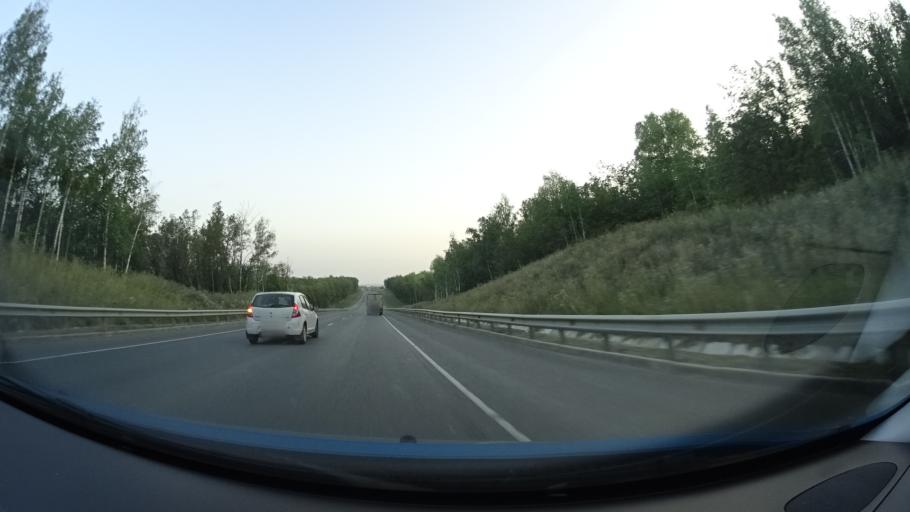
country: RU
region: Samara
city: Sernovodsk
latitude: 53.9214
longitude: 51.3107
